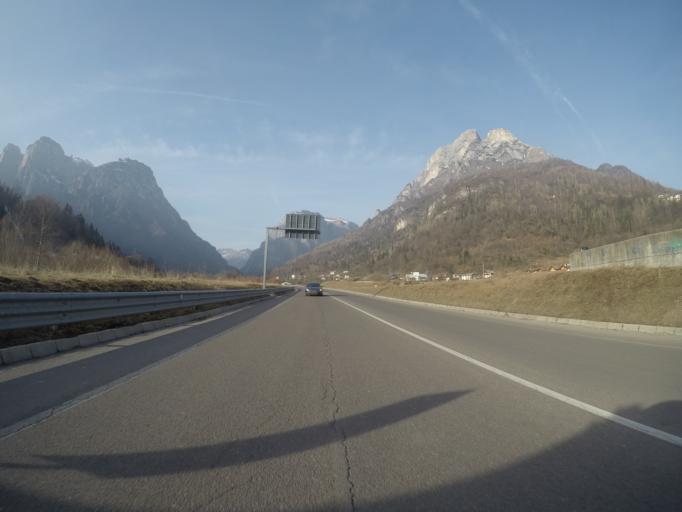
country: IT
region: Veneto
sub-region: Provincia di Belluno
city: Taibon Agordino
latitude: 46.2884
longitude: 12.0230
